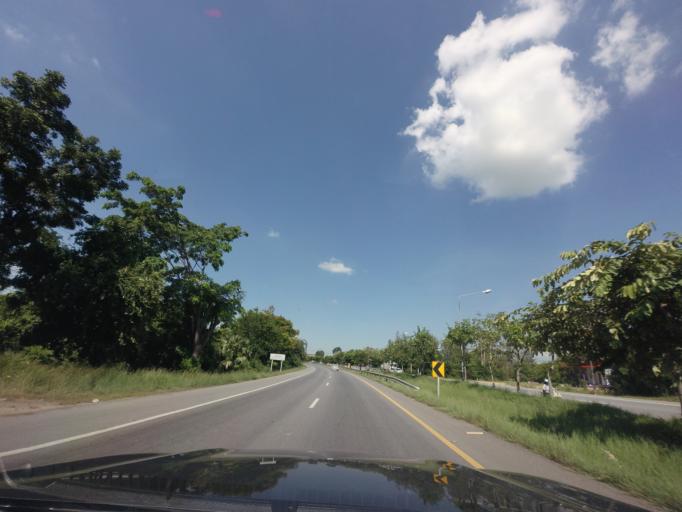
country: TH
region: Nakhon Ratchasima
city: Non Sung
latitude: 15.1458
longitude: 102.3231
